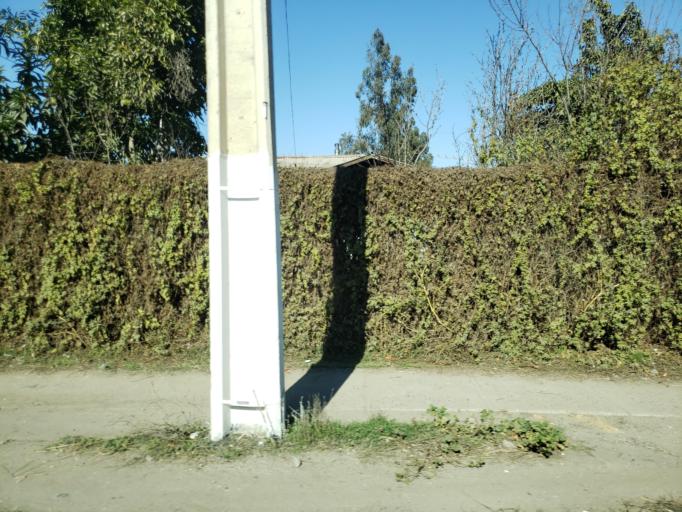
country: CL
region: Santiago Metropolitan
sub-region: Provincia de Talagante
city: El Monte
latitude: -33.6858
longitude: -71.0164
